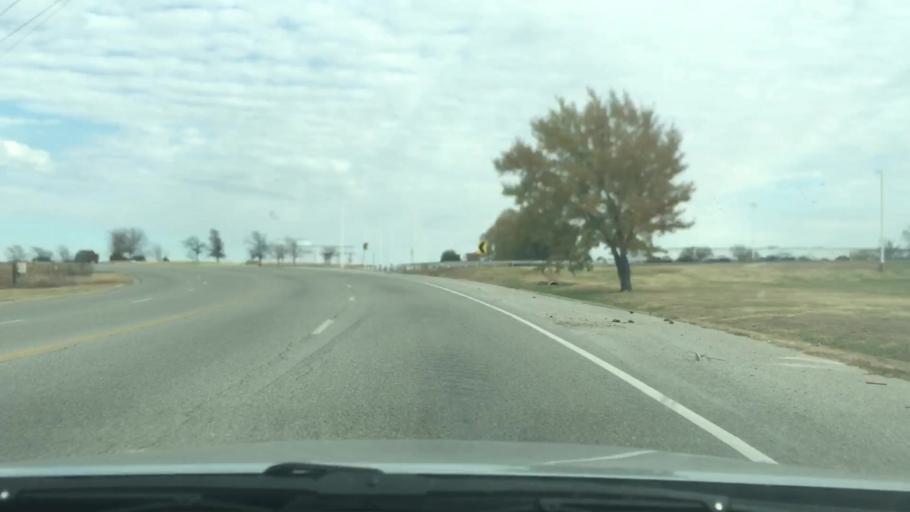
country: US
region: Kansas
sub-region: Sedgwick County
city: Wichita
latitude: 37.6500
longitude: -97.2711
